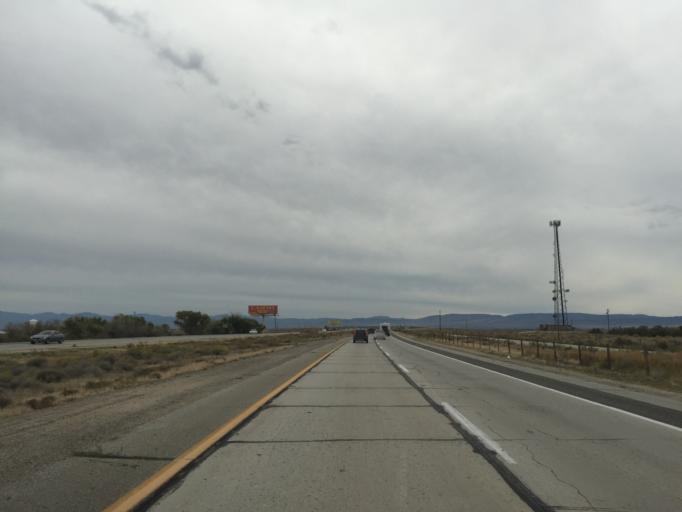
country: US
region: California
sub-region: Kern County
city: Rosamond
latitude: 34.8308
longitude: -118.1704
